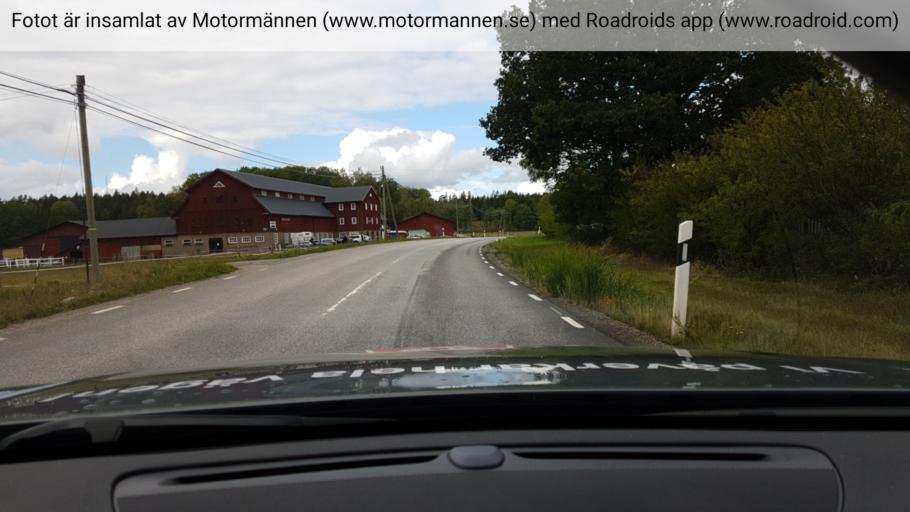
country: SE
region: Stockholm
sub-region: Nykvarns Kommun
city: Nykvarn
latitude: 59.2045
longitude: 17.4017
